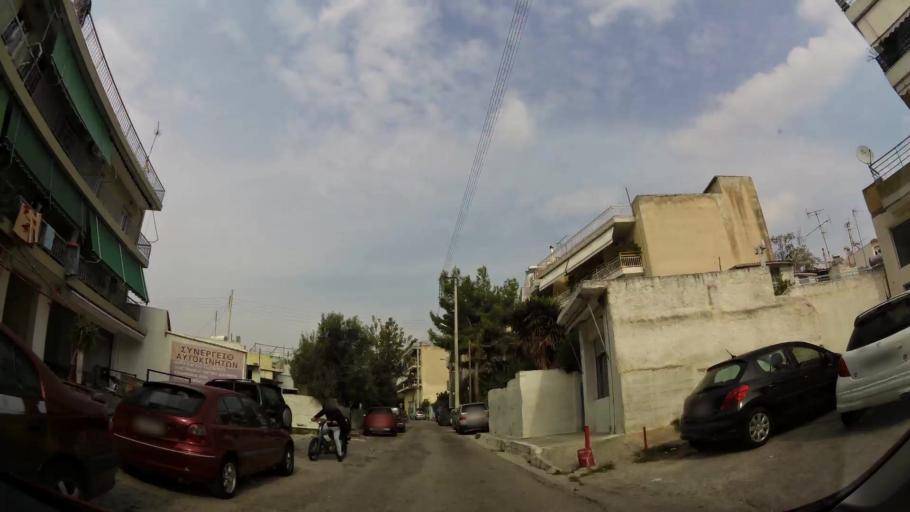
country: GR
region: Attica
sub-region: Nomarchia Athinas
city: Petroupolis
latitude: 38.0269
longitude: 23.6813
